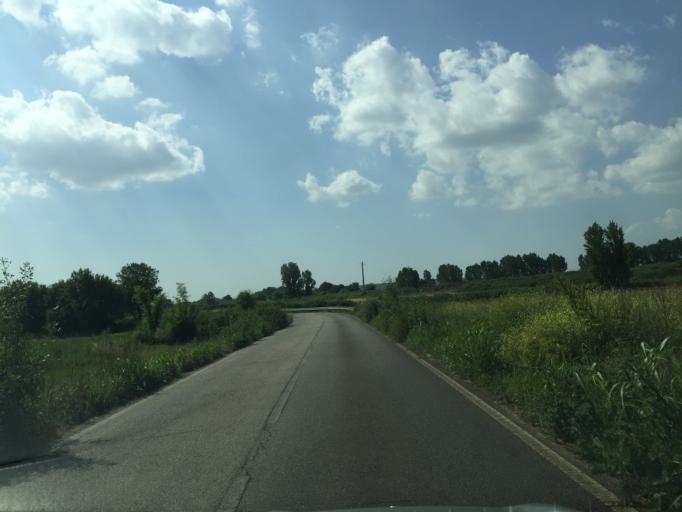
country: PT
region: Santarem
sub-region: Alpiarca
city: Alpiarca
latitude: 39.3018
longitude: -8.5600
